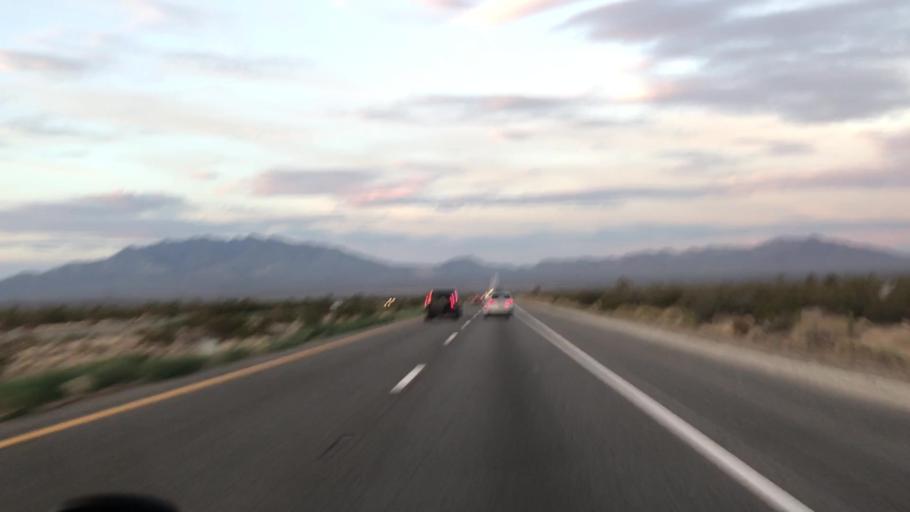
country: US
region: Nevada
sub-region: Clark County
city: Sandy Valley
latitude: 35.4141
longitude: -115.7586
